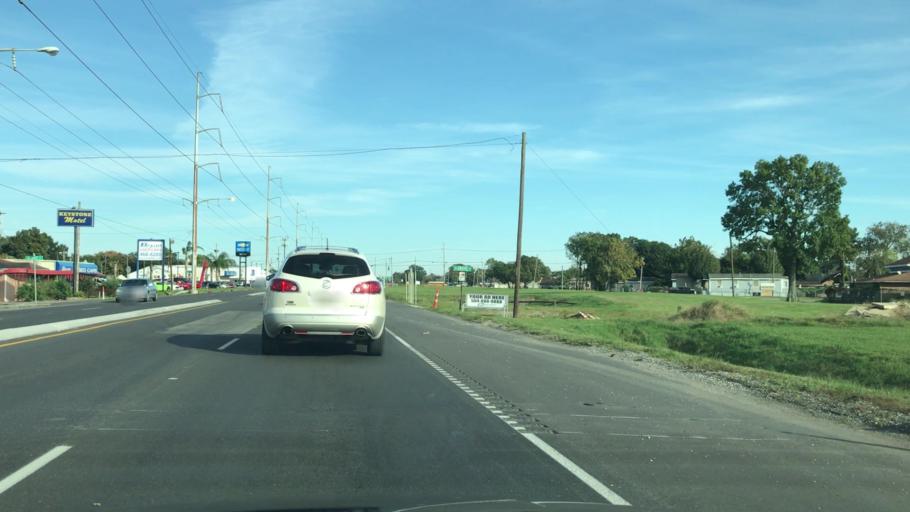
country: US
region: Louisiana
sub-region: Jefferson Parish
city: Kenner
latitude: 29.9792
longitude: -90.2347
